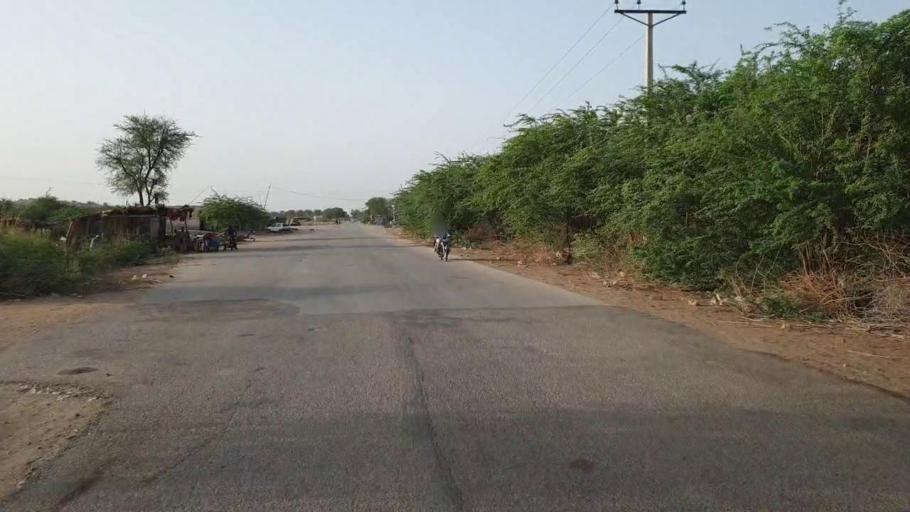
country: PK
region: Sindh
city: Bozdar
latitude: 27.1244
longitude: 68.9570
